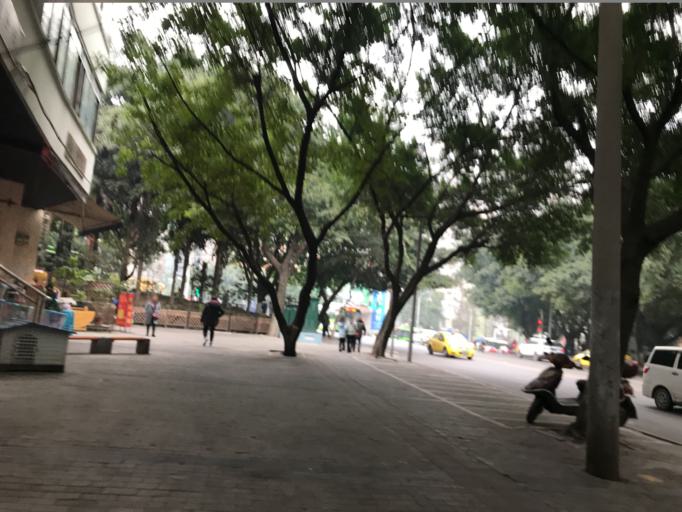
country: CN
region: Chongqing Shi
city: Chongqing
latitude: 29.5305
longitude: 106.5531
